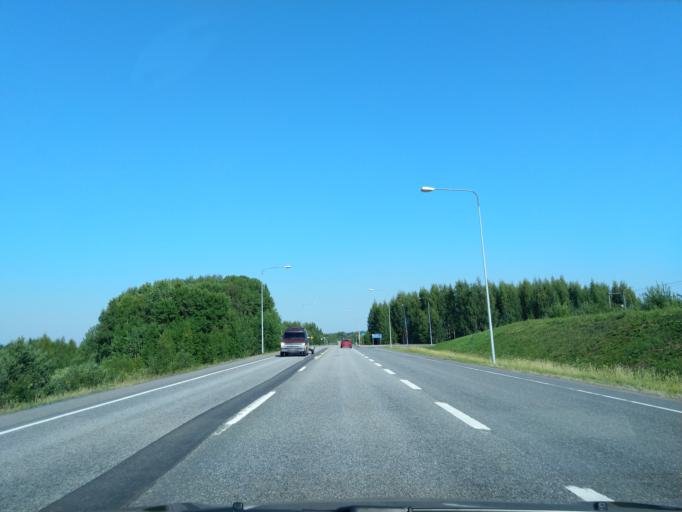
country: FI
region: Haeme
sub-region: Forssa
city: Forssa
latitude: 60.8023
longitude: 23.6177
